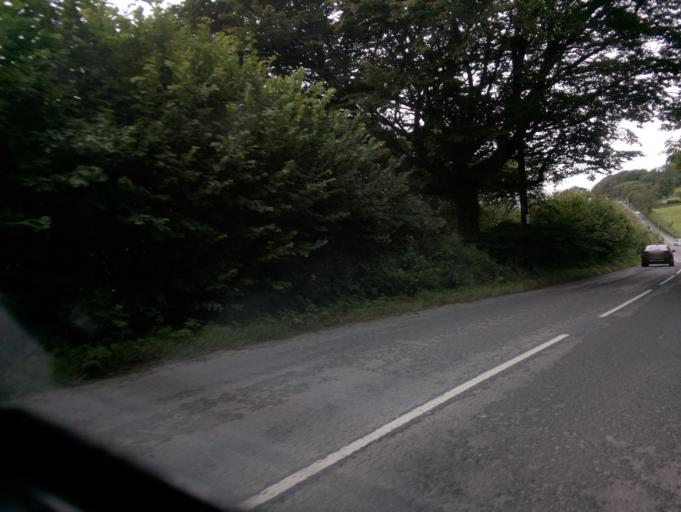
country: GB
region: England
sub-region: Somerset
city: Axbridge
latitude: 51.3042
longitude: -2.7962
